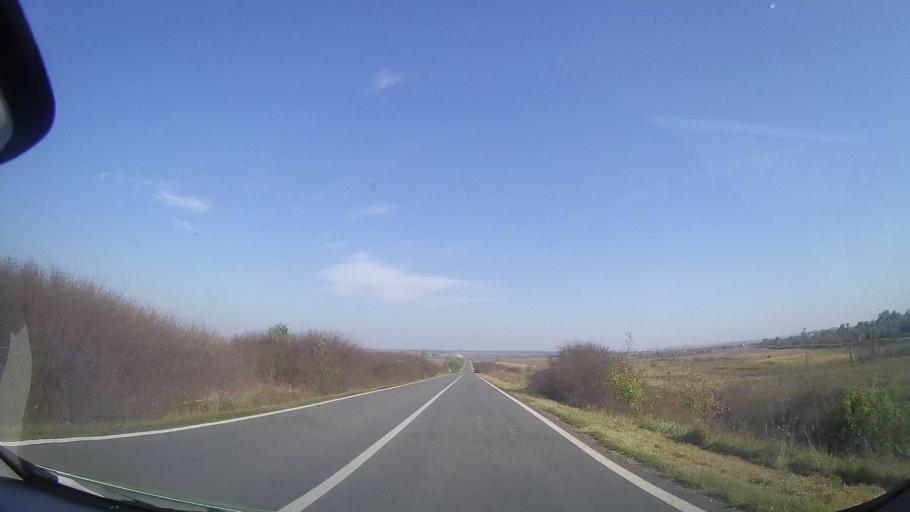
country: RO
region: Timis
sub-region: Comuna Belint
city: Belint
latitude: 45.7669
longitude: 21.7284
